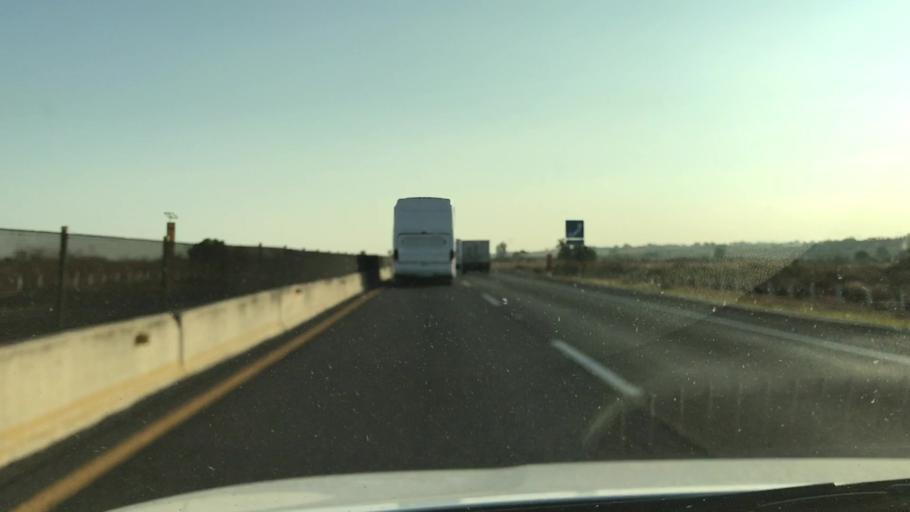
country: MX
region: Jalisco
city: Acatic
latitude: 20.7162
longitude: -102.9460
